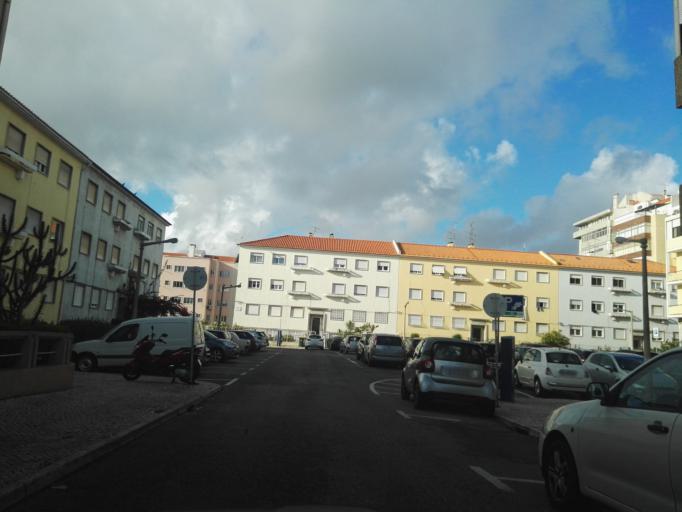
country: PT
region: Lisbon
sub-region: Lisbon
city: Lisbon
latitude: 38.7576
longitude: -9.1386
